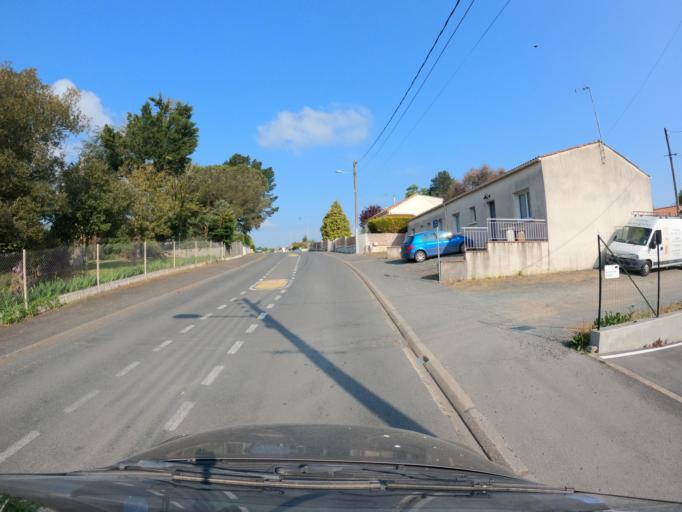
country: FR
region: Pays de la Loire
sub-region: Departement de Maine-et-Loire
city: La Romagne
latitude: 47.0627
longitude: -1.0262
